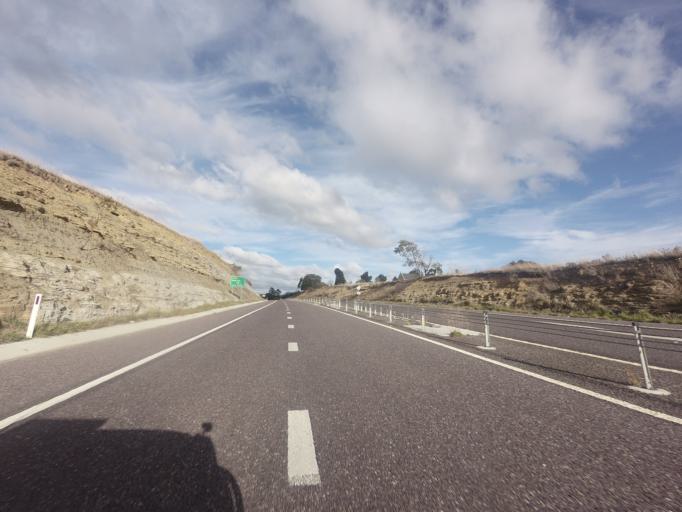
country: AU
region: Tasmania
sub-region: Brighton
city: Bridgewater
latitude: -42.5699
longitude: 147.2110
